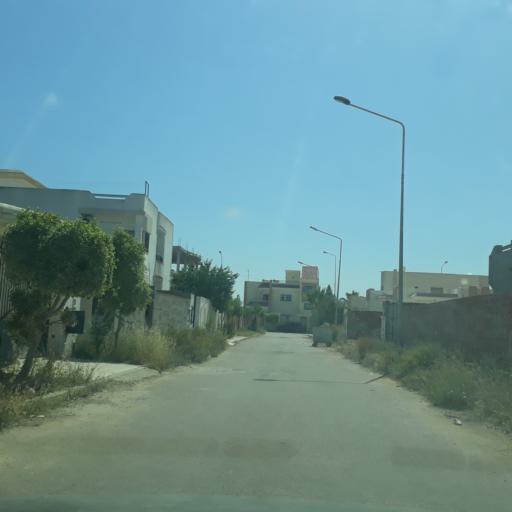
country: TN
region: Safaqis
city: Al Qarmadah
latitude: 34.8327
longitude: 10.7606
